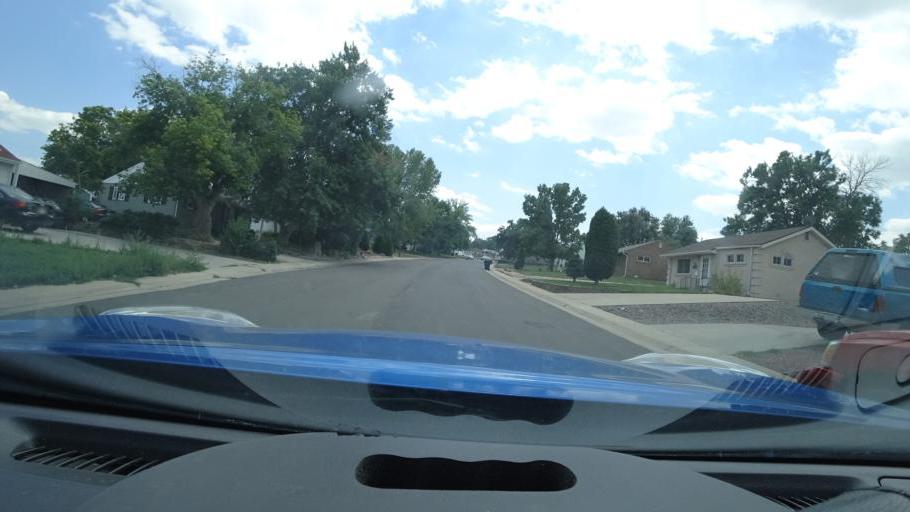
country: US
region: Colorado
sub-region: Arapahoe County
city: Sheridan
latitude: 39.6873
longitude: -105.0105
